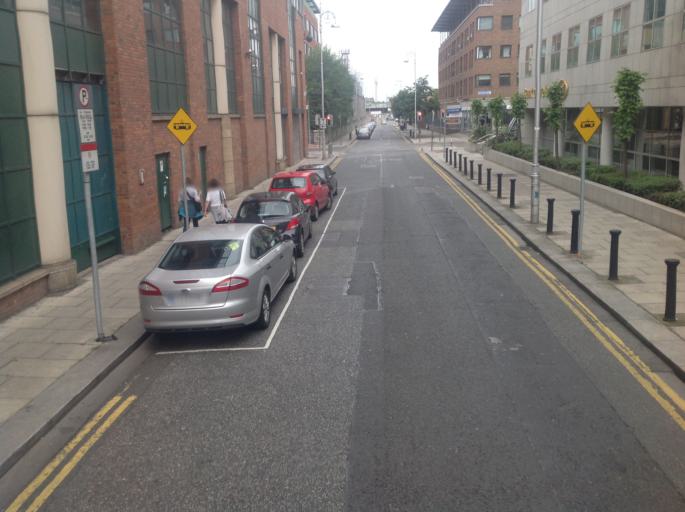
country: IE
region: Leinster
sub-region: Dublin City
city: Dublin
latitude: 53.3487
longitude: -6.2460
